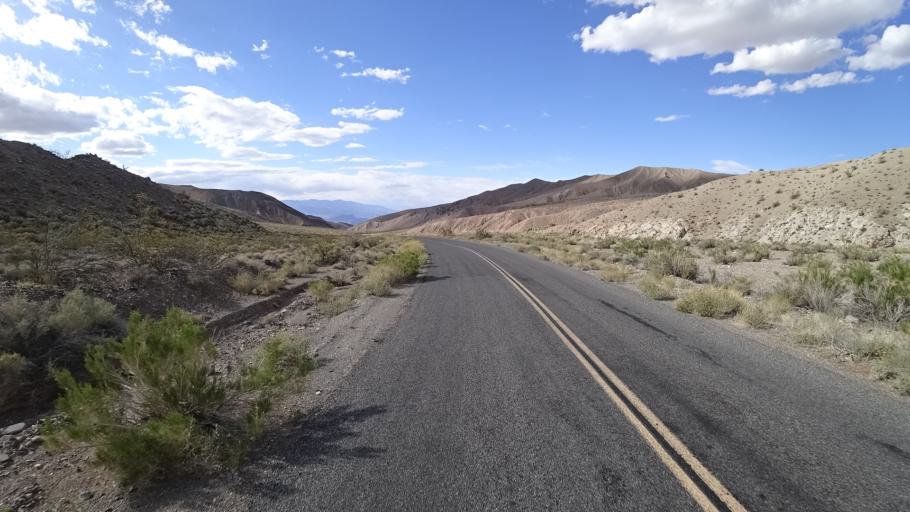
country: US
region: Nevada
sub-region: Nye County
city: Beatty
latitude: 36.4384
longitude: -117.1953
